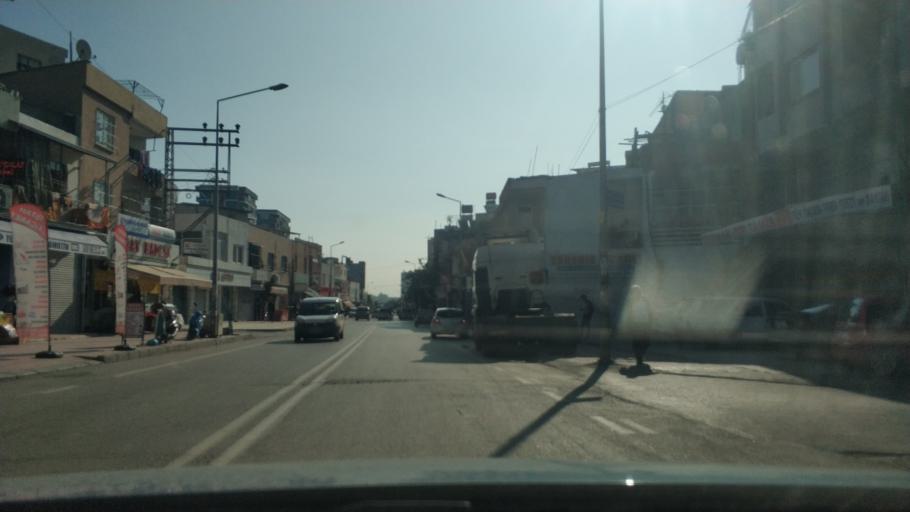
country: TR
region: Adana
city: Seyhan
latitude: 37.0179
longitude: 35.2986
